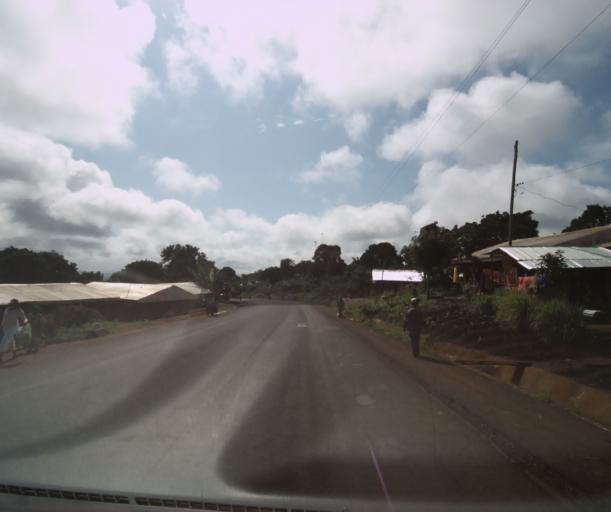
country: CM
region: West
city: Bafoussam
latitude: 5.4820
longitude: 10.4845
